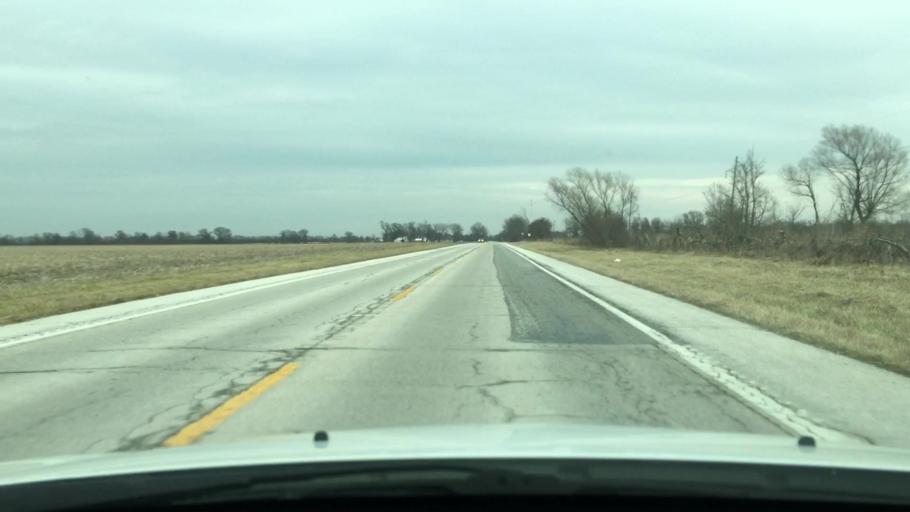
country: US
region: Missouri
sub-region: Audrain County
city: Vandalia
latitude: 39.3292
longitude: -91.4414
